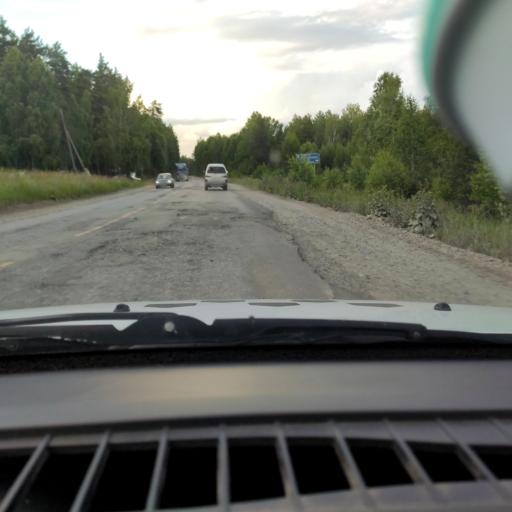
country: RU
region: Chelyabinsk
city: Karabash
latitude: 55.5278
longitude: 60.3386
